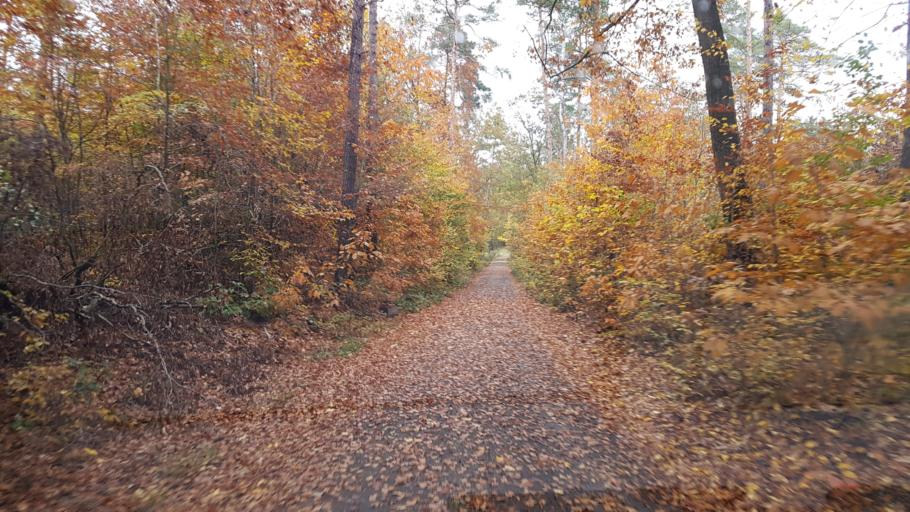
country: DE
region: Saxony
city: Dahlen
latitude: 51.4058
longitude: 12.9838
